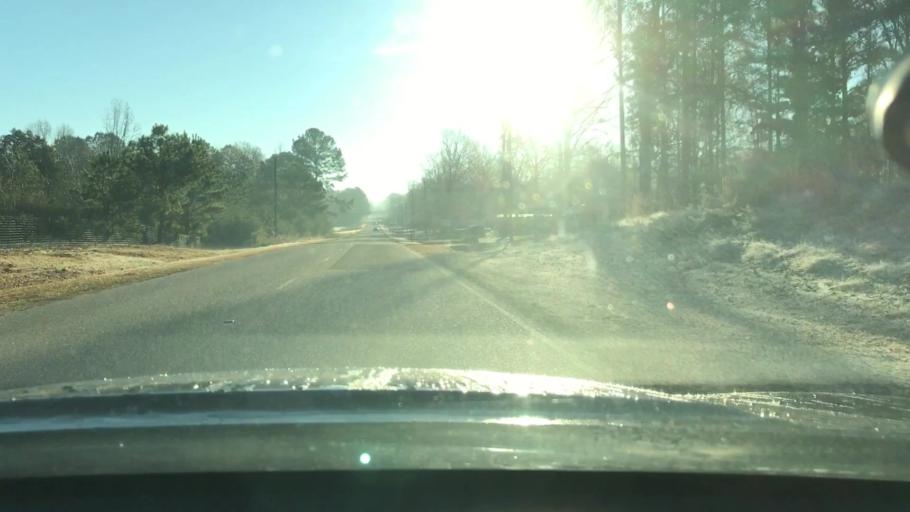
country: US
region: Alabama
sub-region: Talladega County
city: Mignon
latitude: 33.2139
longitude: -86.3027
